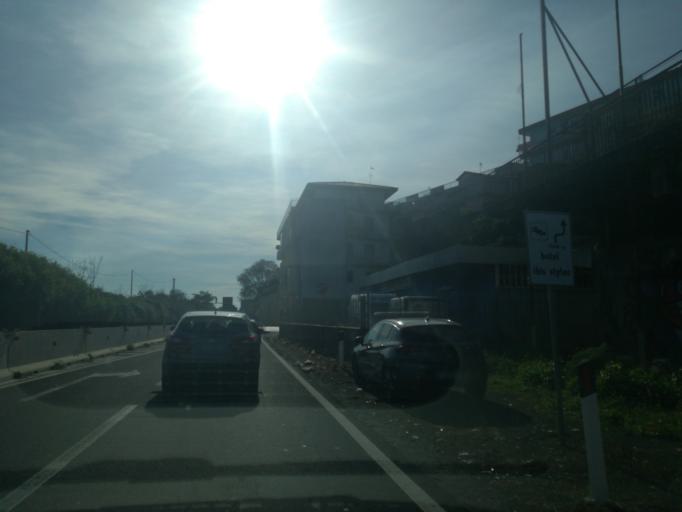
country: IT
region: Sicily
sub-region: Catania
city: Acireale
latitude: 37.6033
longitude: 15.1689
